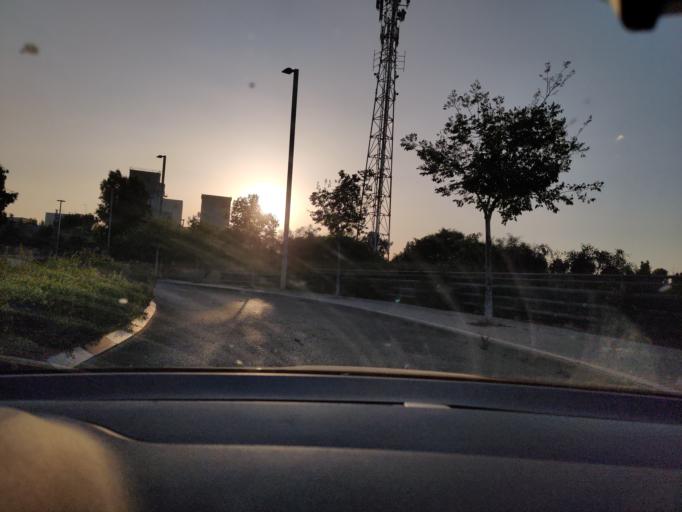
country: IL
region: Haifa
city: Hadera
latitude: 32.4797
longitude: 34.9556
